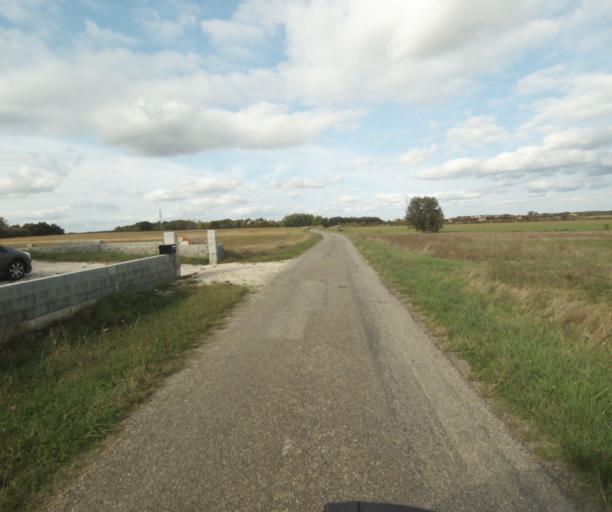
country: FR
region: Midi-Pyrenees
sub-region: Departement du Tarn-et-Garonne
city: Verdun-sur-Garonne
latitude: 43.8388
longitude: 1.1605
